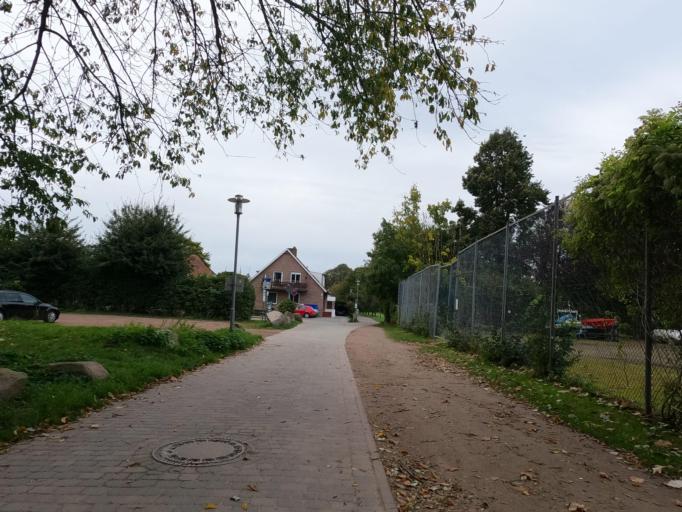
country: DE
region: Schleswig-Holstein
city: Kellenhusen
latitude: 54.1936
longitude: 11.0691
